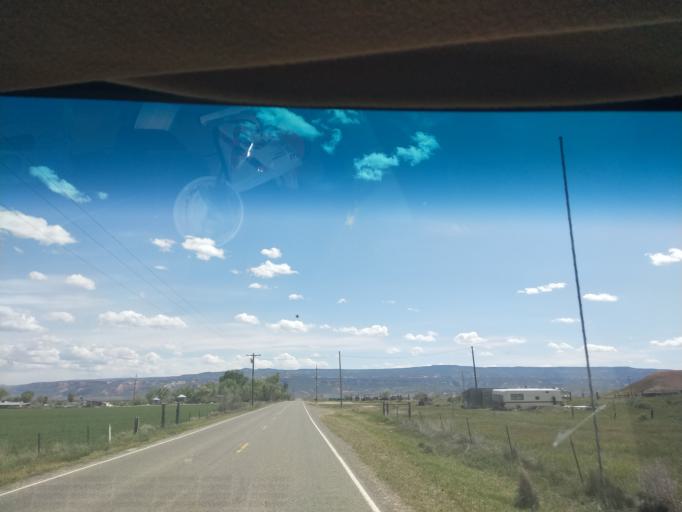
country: US
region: Colorado
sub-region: Mesa County
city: Fruita
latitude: 39.2003
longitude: -108.7570
